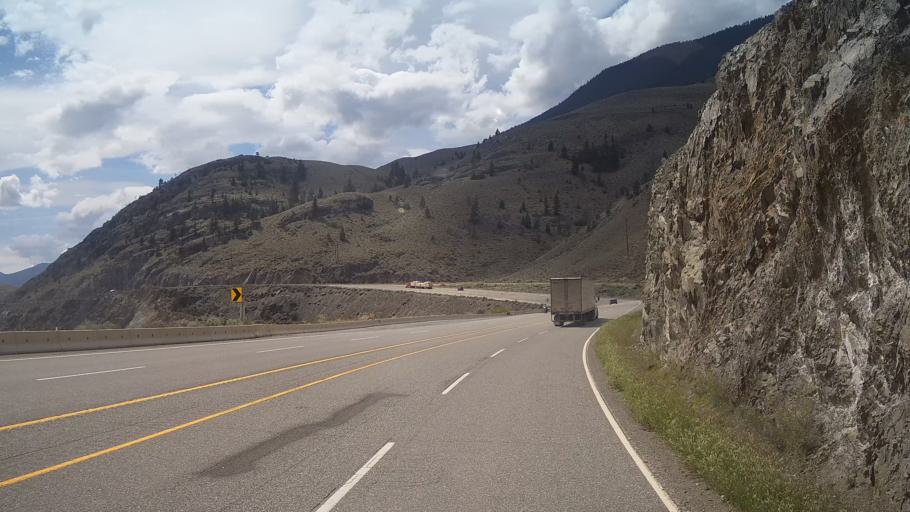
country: CA
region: British Columbia
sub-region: Thompson-Nicola Regional District
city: Ashcroft
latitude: 50.5110
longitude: -121.2837
